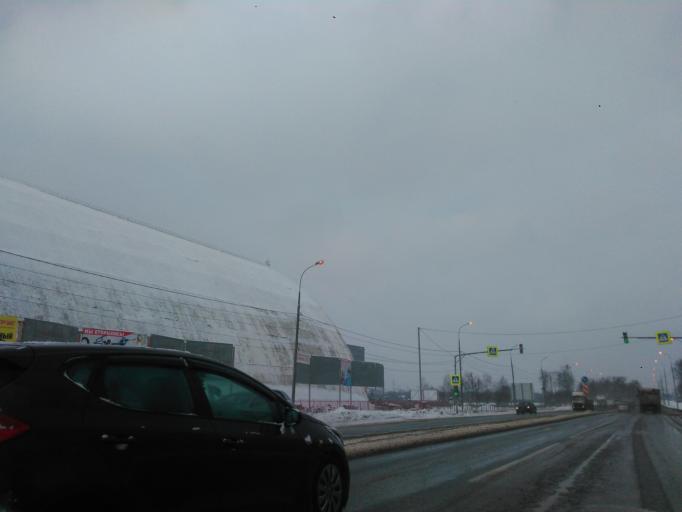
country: RU
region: Moskovskaya
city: Podosinki
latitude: 56.2082
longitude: 37.5227
